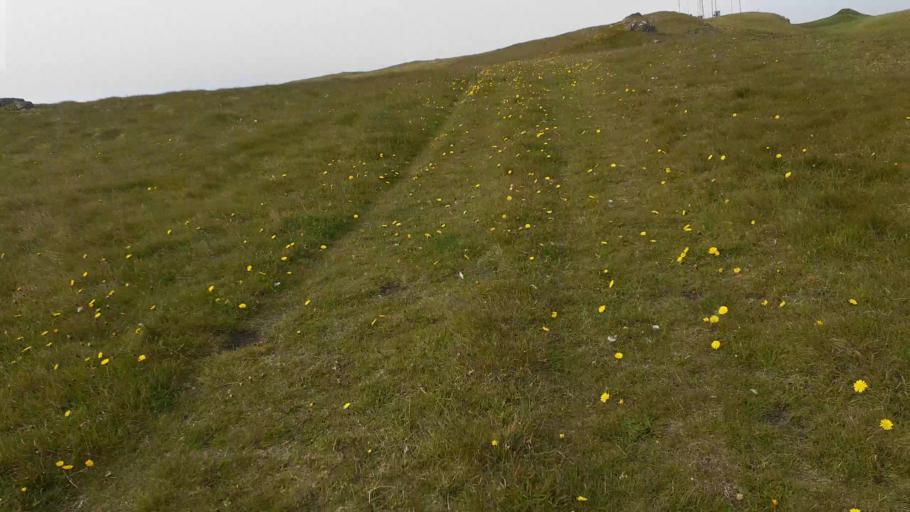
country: IS
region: Northeast
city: Dalvik
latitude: 66.5422
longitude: -17.9919
